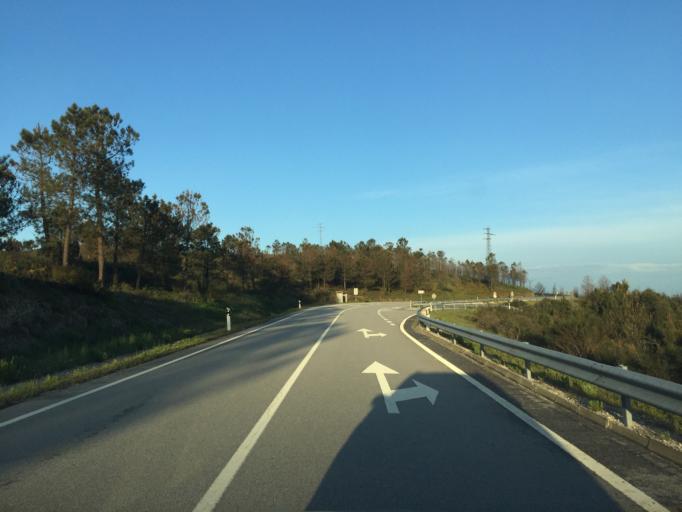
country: PT
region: Coimbra
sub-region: Gois
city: Gois
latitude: 40.1105
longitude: -8.0295
